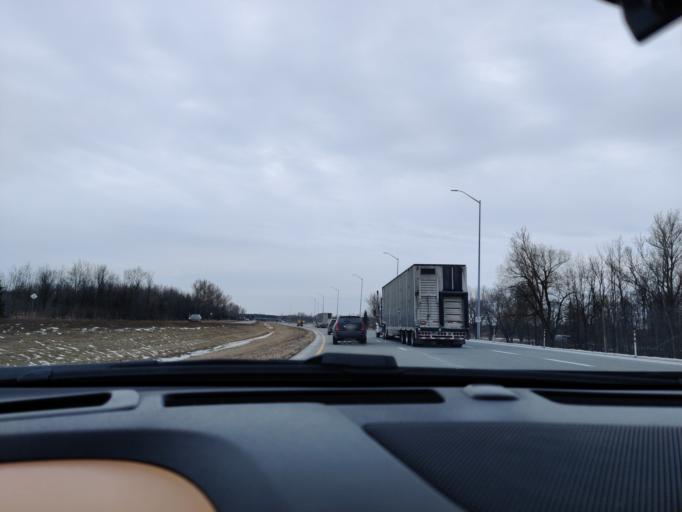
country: US
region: New York
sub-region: St. Lawrence County
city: Massena
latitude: 44.9767
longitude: -75.0787
